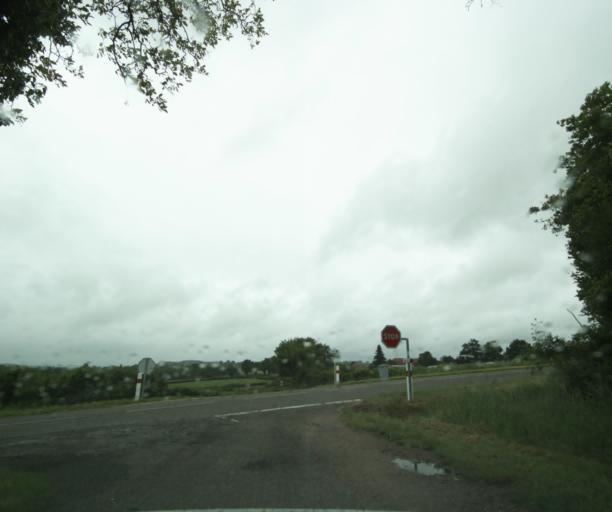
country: FR
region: Bourgogne
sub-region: Departement de Saone-et-Loire
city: Saint-Vallier
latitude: 46.5008
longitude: 4.4544
